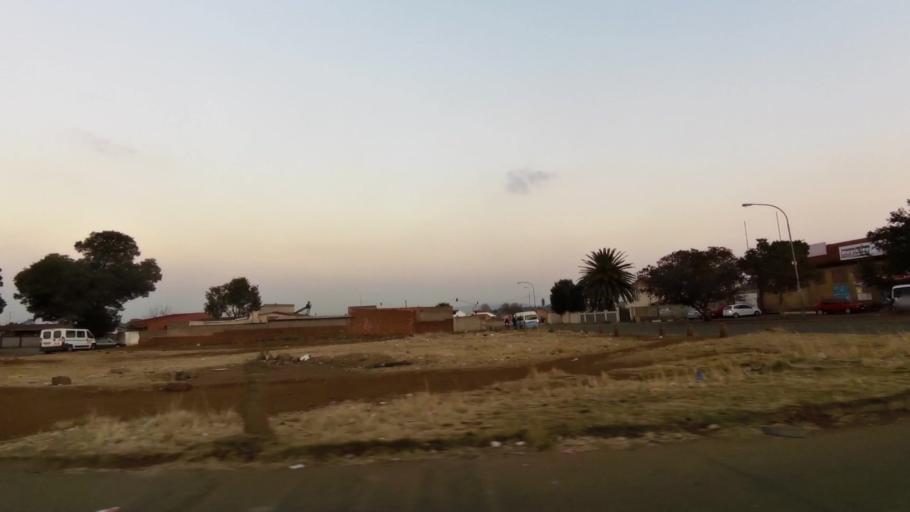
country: ZA
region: Gauteng
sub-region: City of Johannesburg Metropolitan Municipality
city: Soweto
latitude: -26.2930
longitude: 27.8752
